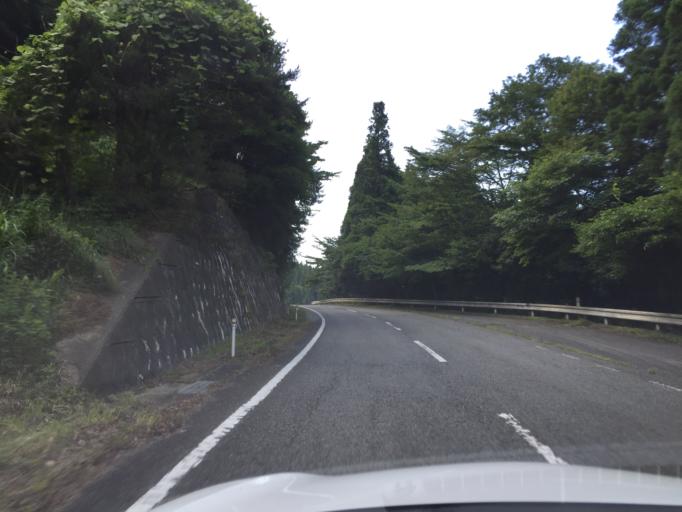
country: JP
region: Fukushima
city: Ishikawa
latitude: 37.1346
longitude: 140.6417
